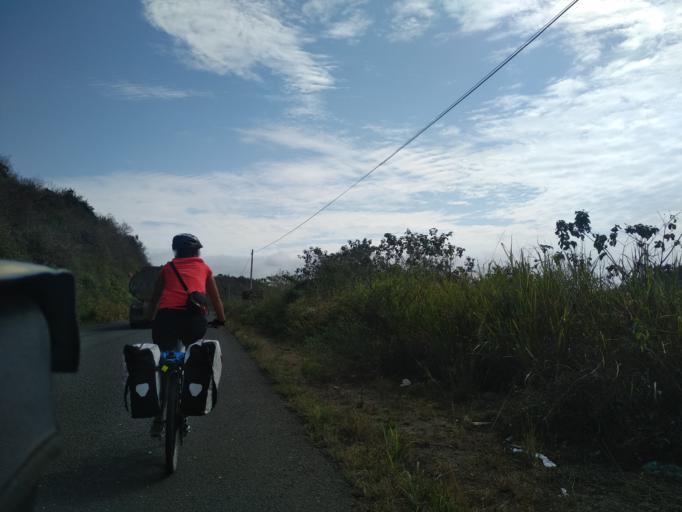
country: EC
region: Manabi
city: Jipijapa
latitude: -1.4461
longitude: -80.7566
